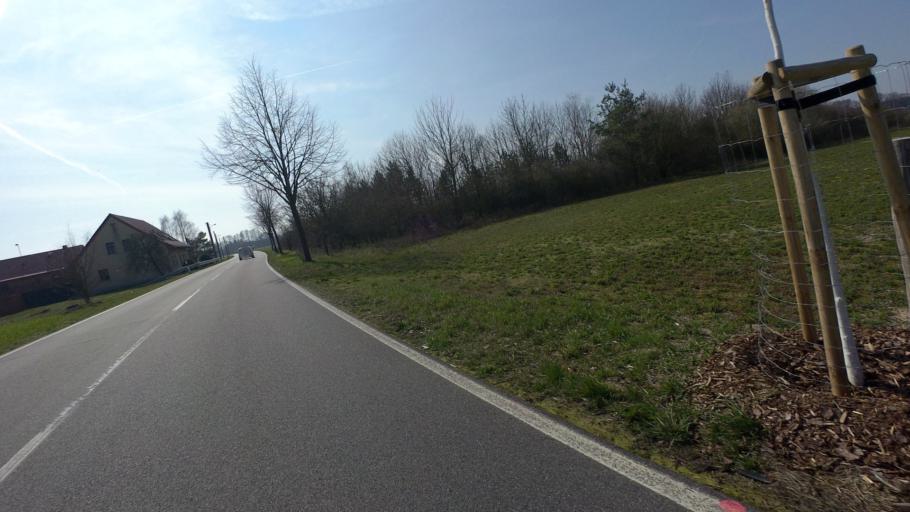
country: DE
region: Brandenburg
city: Golssen
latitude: 51.9444
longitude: 13.5989
